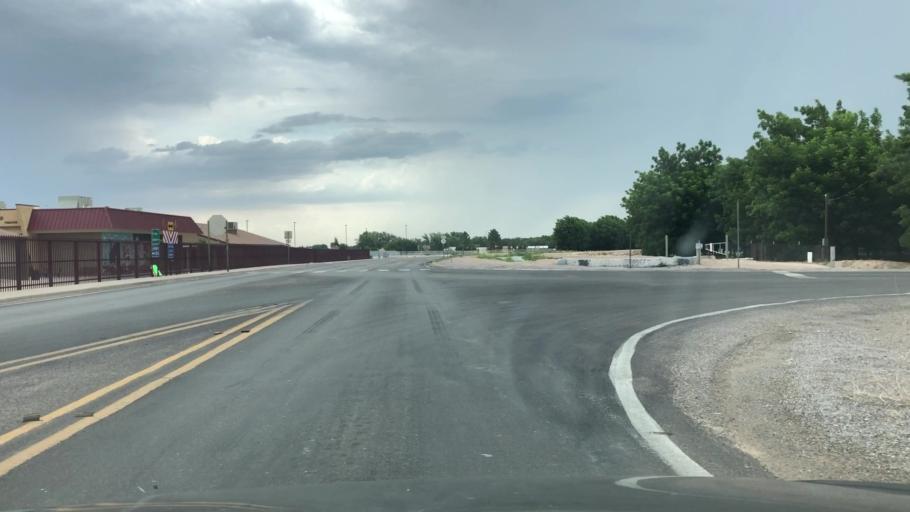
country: US
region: New Mexico
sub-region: Dona Ana County
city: La Union
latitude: 31.9974
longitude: -106.6553
